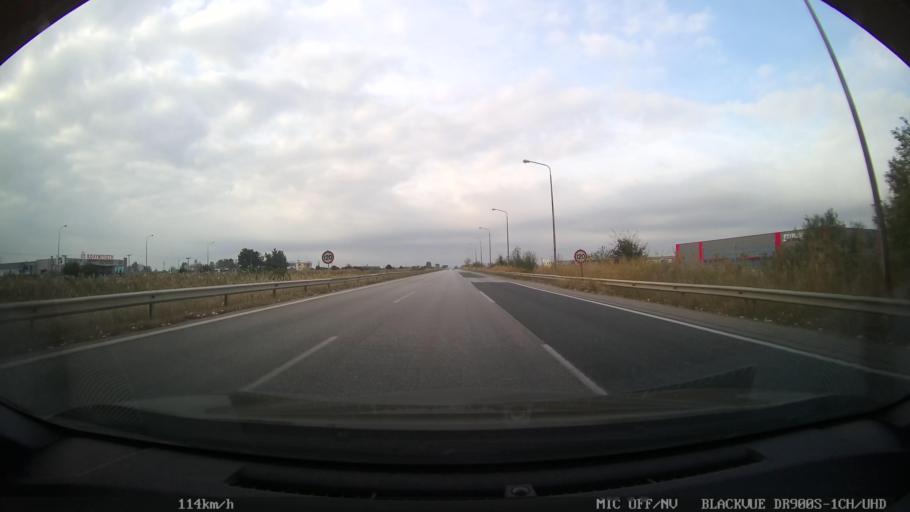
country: GR
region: Central Macedonia
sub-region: Nomos Thessalonikis
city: Sindos
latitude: 40.6449
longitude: 22.8027
